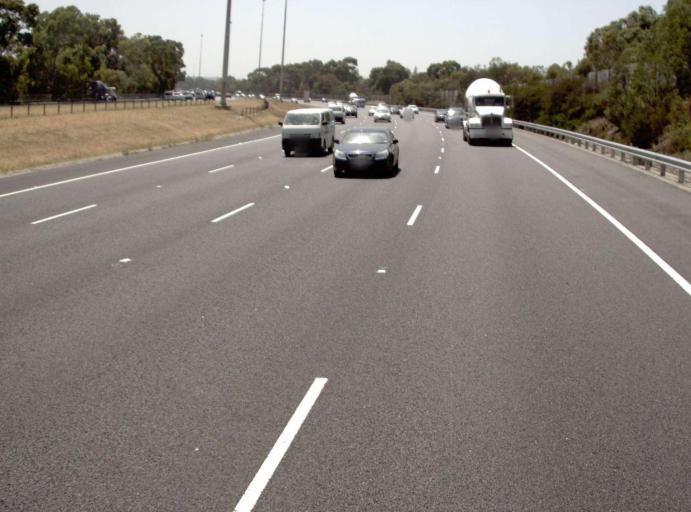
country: AU
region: Victoria
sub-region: Boroondara
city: Kew East
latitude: -37.7909
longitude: 145.0506
